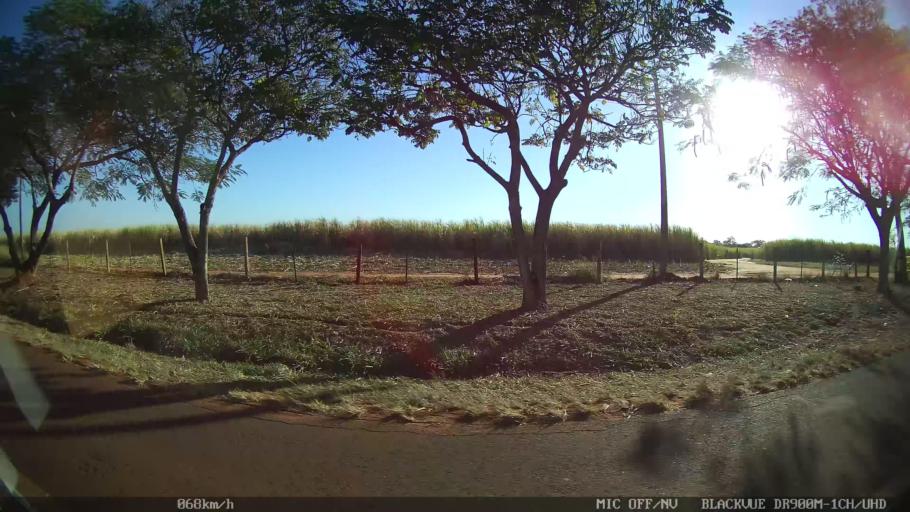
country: BR
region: Sao Paulo
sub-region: Guapiacu
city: Guapiacu
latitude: -20.7766
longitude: -49.2248
